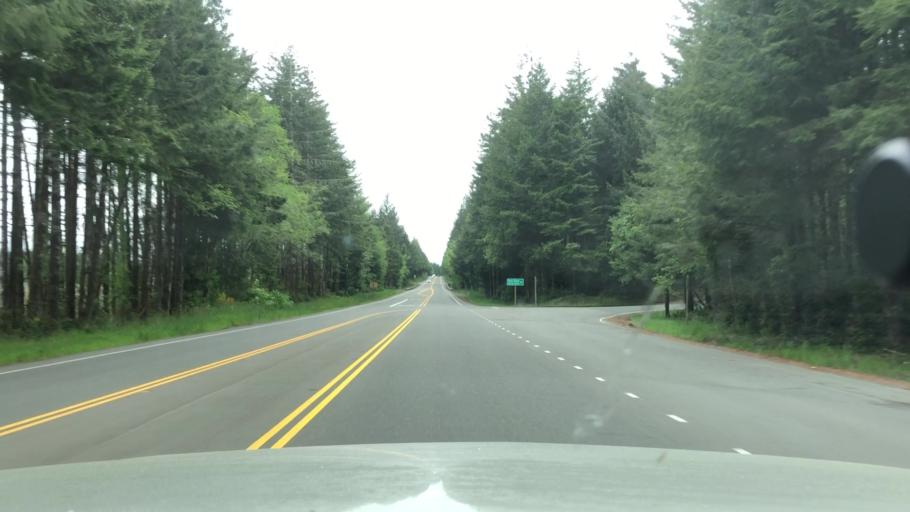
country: US
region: Oregon
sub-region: Coos County
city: Coquille
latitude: 43.2034
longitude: -124.3081
